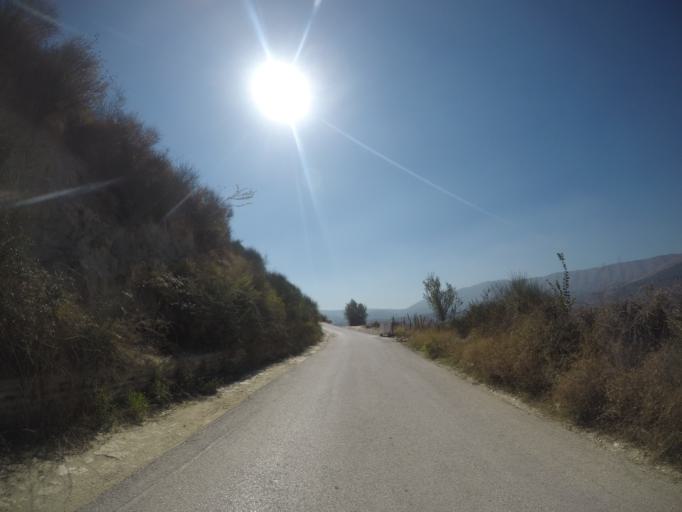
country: AL
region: Berat
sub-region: Rrethi i Beratit
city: Berat
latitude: 40.7155
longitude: 19.9445
